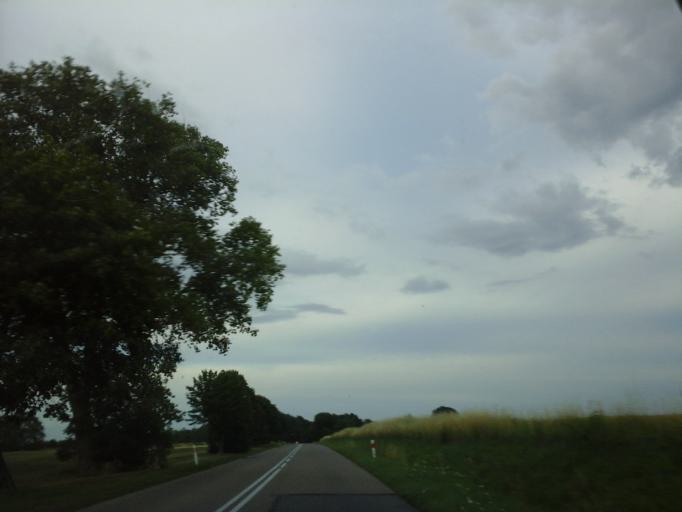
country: PL
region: West Pomeranian Voivodeship
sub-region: Powiat goleniowski
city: Nowogard
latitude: 53.6972
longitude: 15.0574
